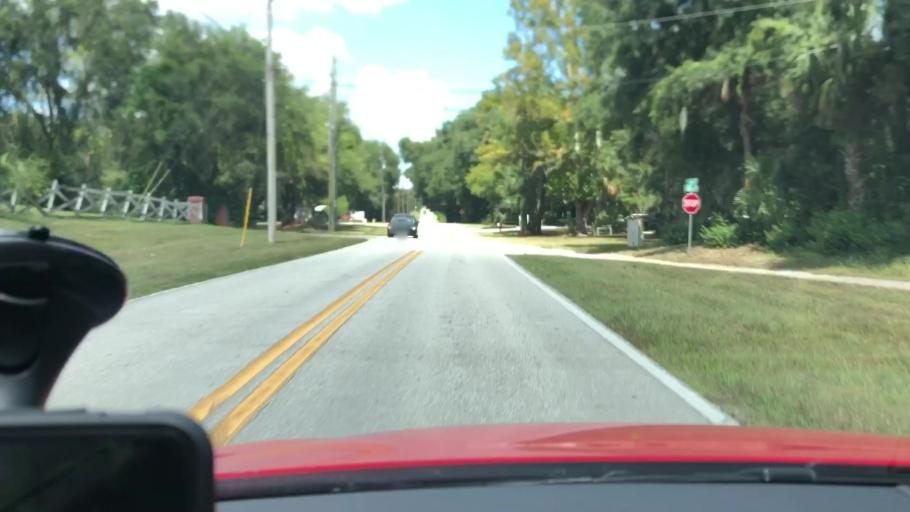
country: US
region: Florida
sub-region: Volusia County
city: North DeLand
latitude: 29.0488
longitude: -81.3165
